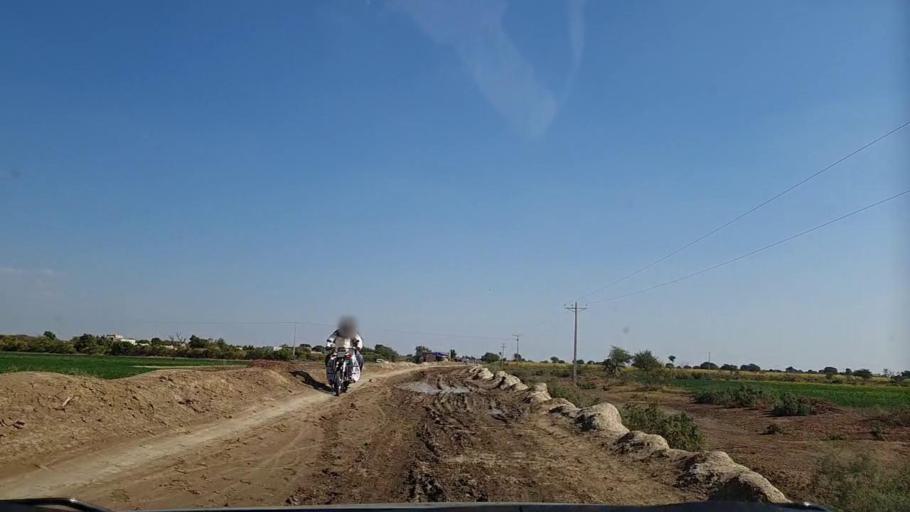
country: PK
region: Sindh
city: Pithoro
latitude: 25.6894
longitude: 69.4371
